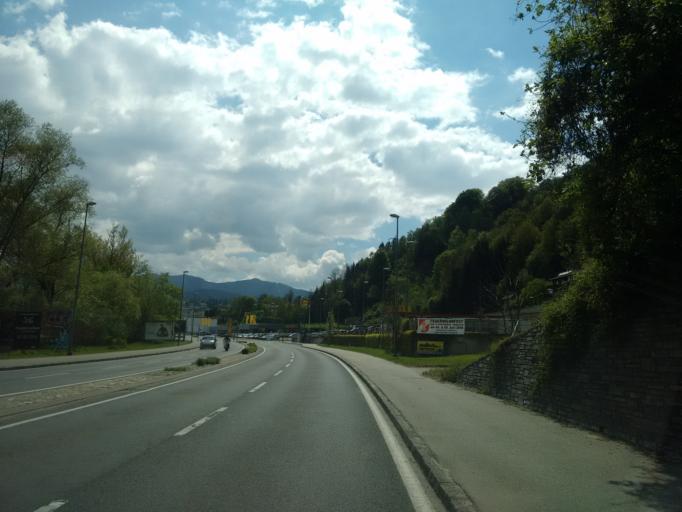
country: AT
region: Styria
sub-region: Politischer Bezirk Bruck-Muerzzuschlag
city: Bruck an der Mur
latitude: 47.4309
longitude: 15.2684
